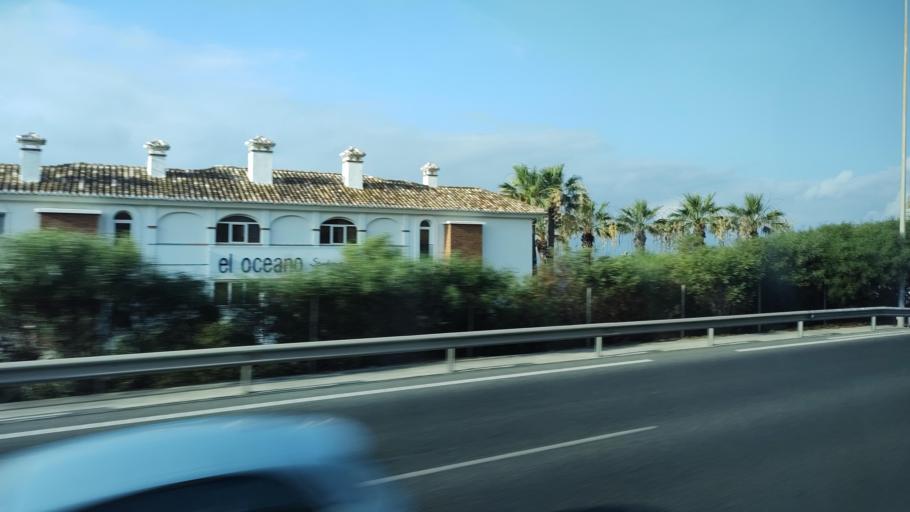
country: ES
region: Andalusia
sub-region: Provincia de Malaga
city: Fuengirola
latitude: 36.4913
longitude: -4.6952
